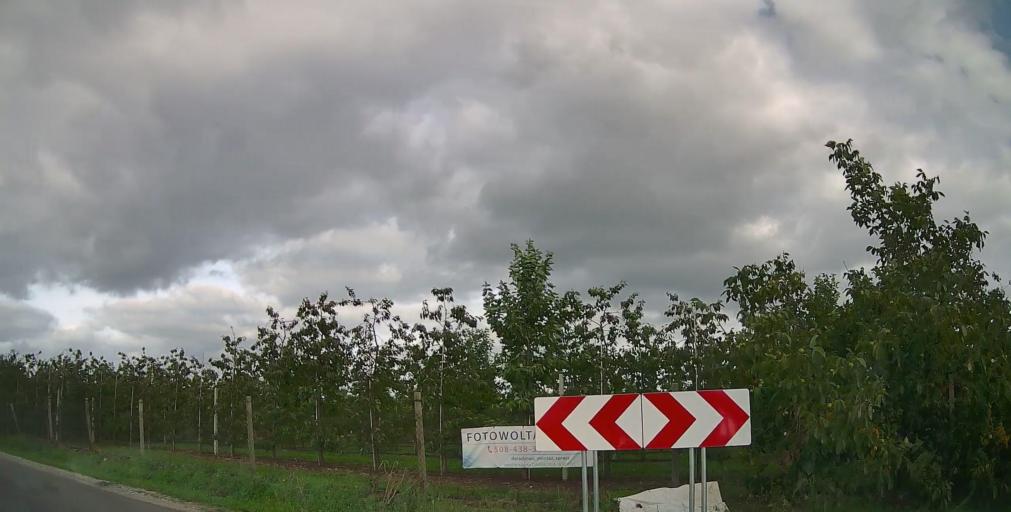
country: PL
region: Masovian Voivodeship
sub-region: Powiat bialobrzeski
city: Promna
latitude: 51.7091
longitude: 20.9581
